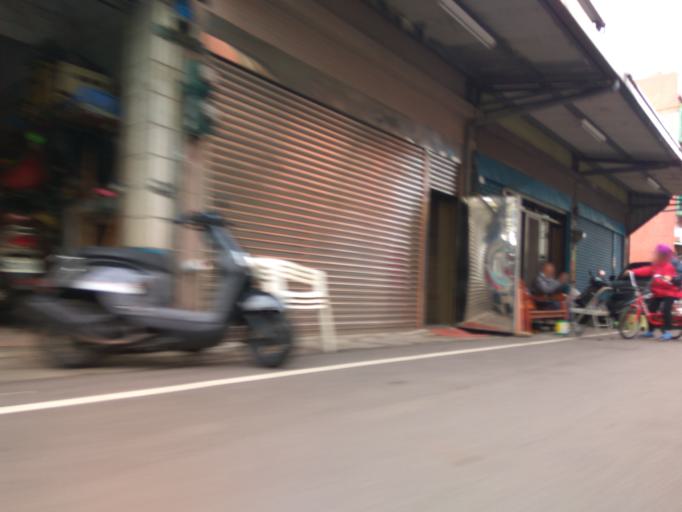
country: TW
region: Taiwan
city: Daxi
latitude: 24.9246
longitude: 121.2051
